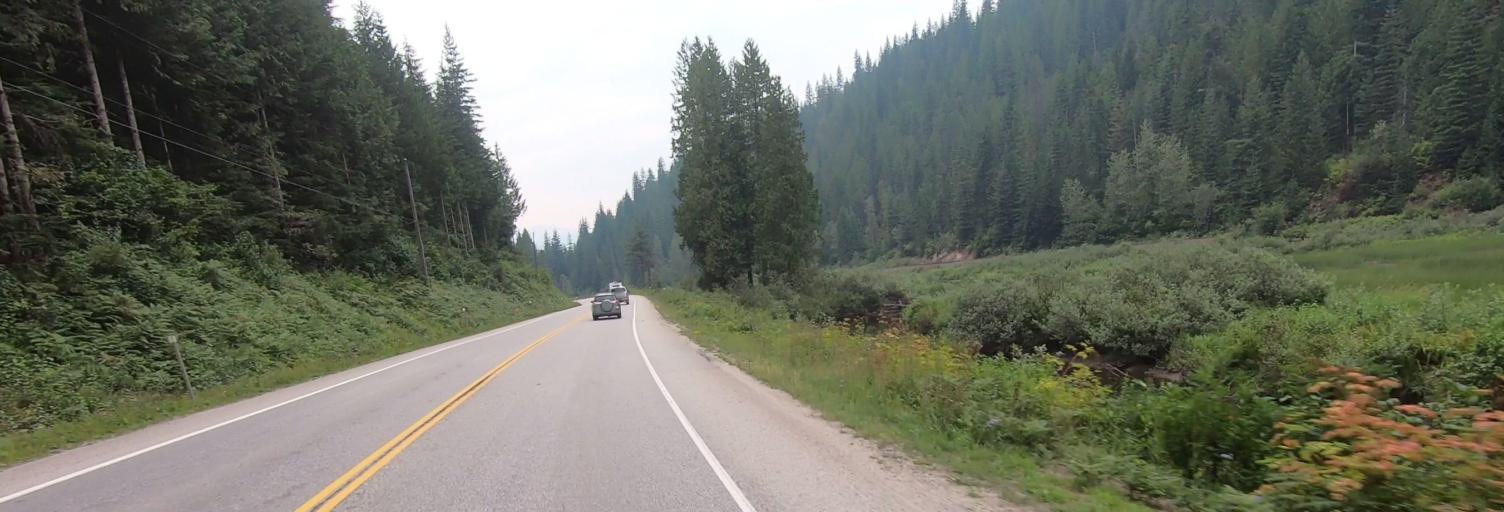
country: CA
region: British Columbia
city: Revelstoke
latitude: 50.9724
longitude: -118.5961
